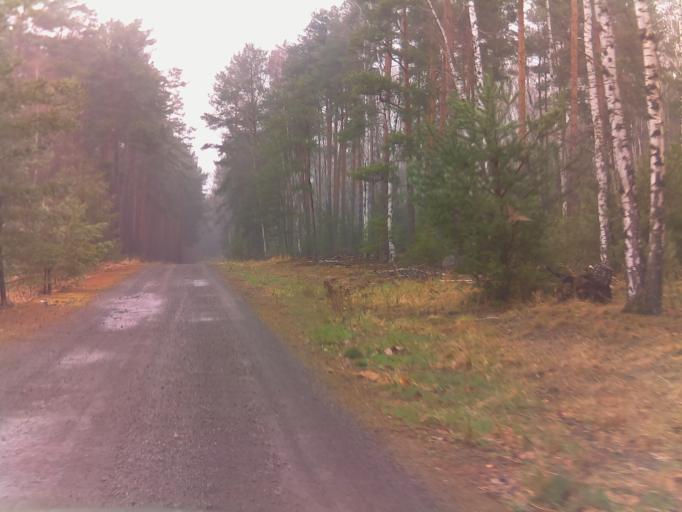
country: DE
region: Brandenburg
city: Jamlitz
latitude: 52.0535
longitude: 14.3592
